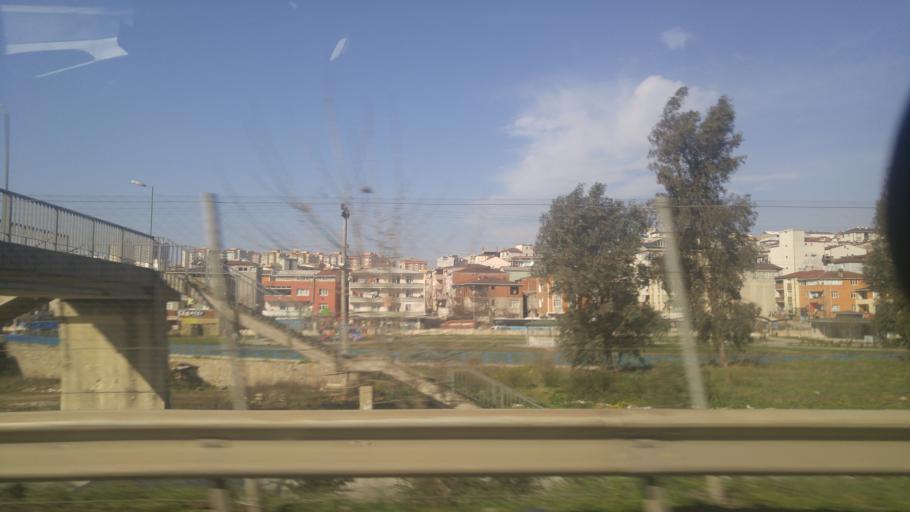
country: TR
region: Kocaeli
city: Darica
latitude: 40.8280
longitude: 29.3658
